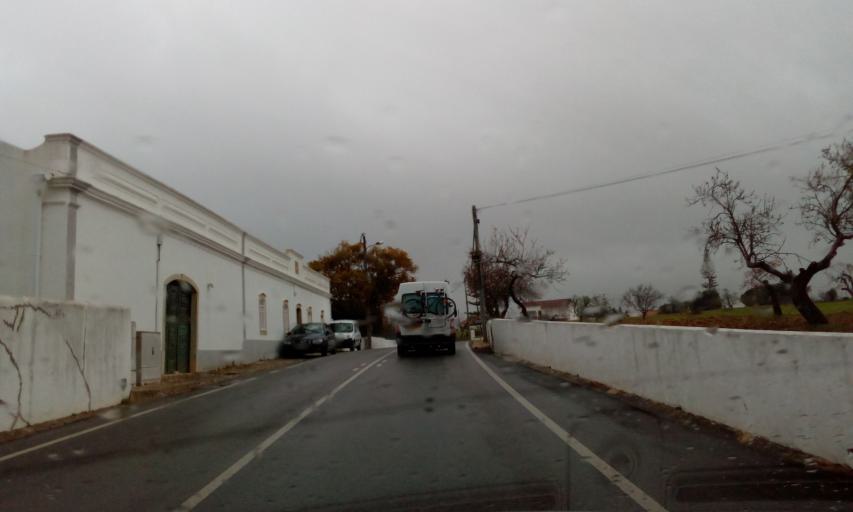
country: PT
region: Faro
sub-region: Albufeira
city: Guia
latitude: 37.1239
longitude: -8.2953
